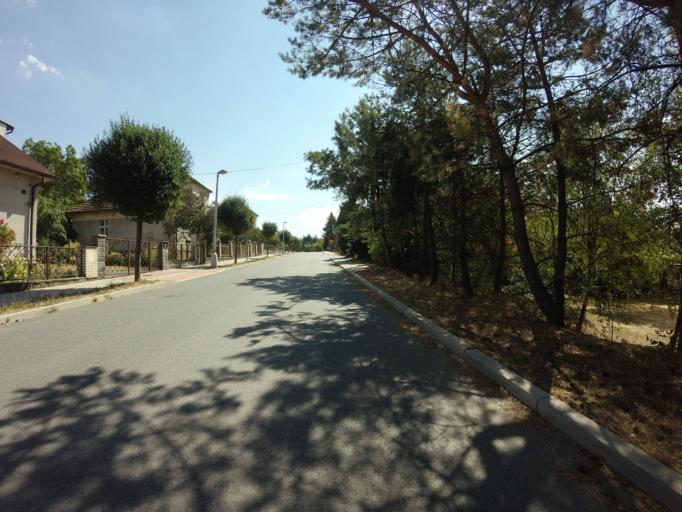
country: CZ
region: Central Bohemia
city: Jilove u Prahy
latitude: 49.8972
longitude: 14.4904
